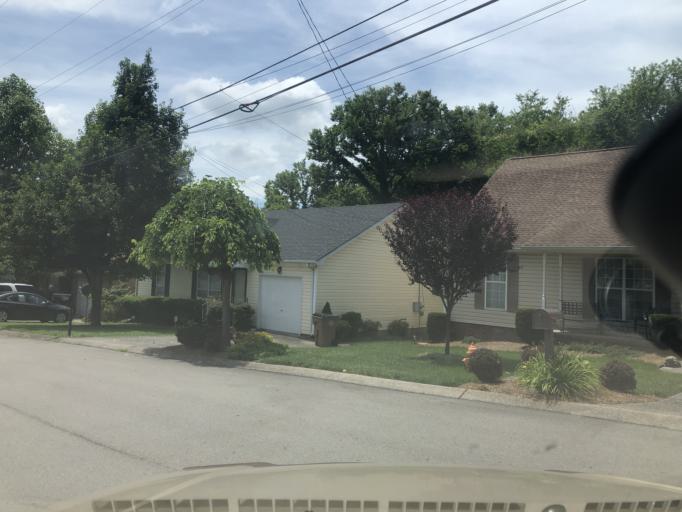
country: US
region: Tennessee
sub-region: Davidson County
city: Lakewood
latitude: 36.2538
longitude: -86.7033
